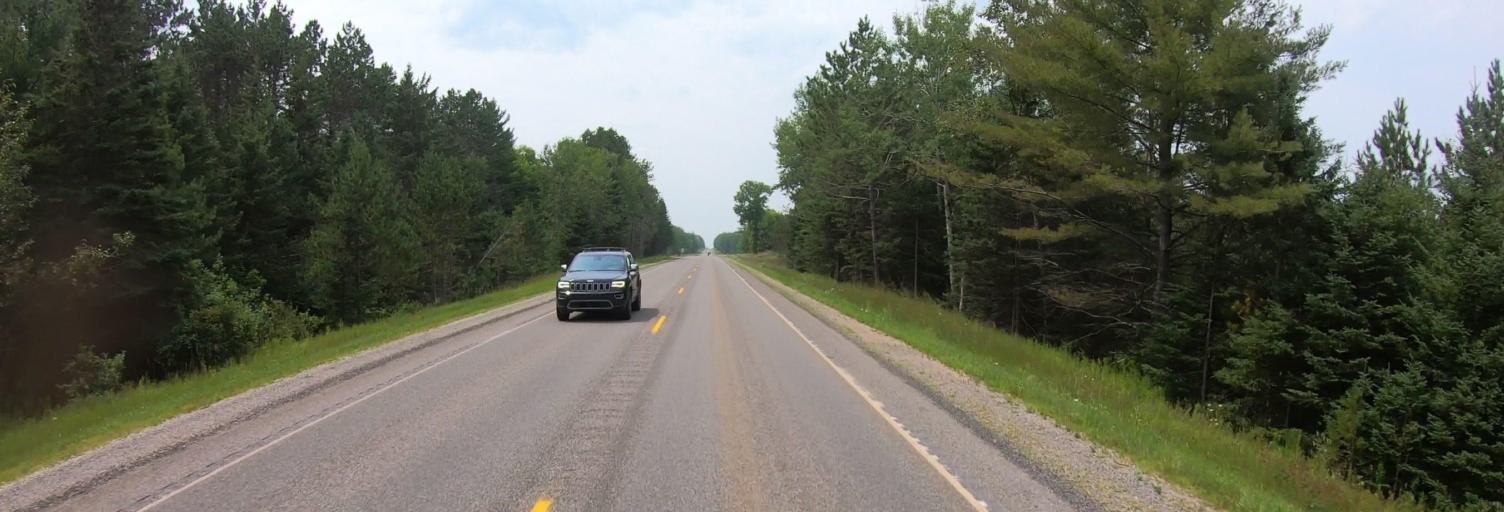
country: US
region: Michigan
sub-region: Alger County
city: Munising
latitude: 46.3329
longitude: -86.7767
